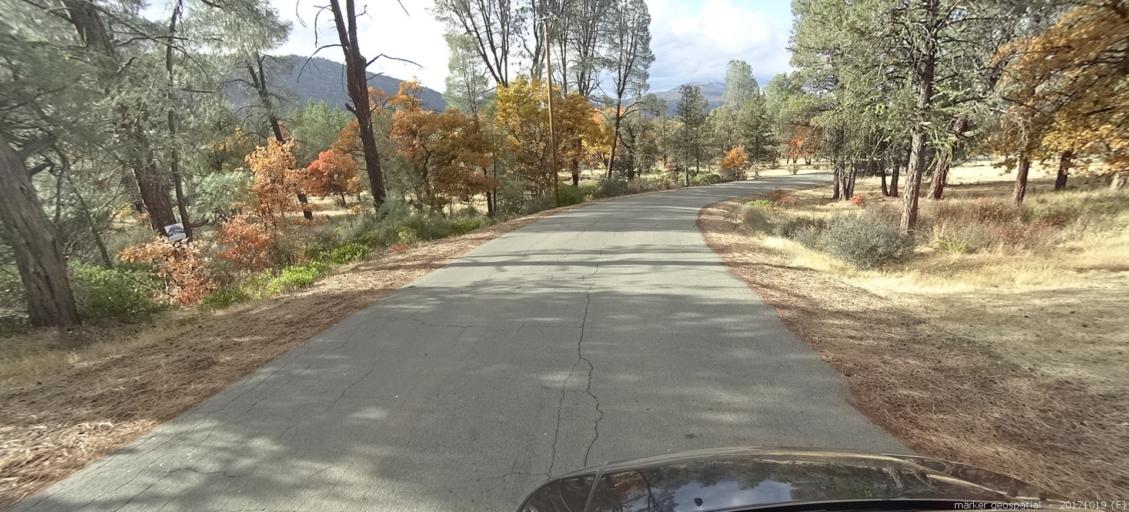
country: US
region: California
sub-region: Shasta County
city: Burney
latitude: 40.9629
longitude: -121.4403
